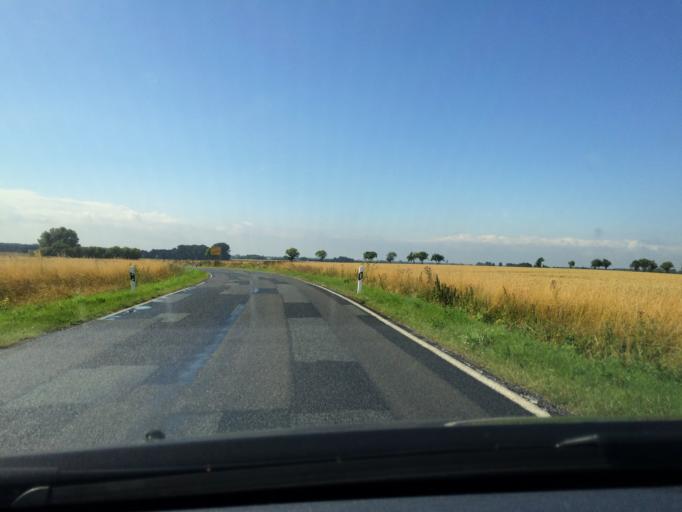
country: DE
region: Mecklenburg-Vorpommern
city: Altenpleen
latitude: 54.3709
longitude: 12.9327
